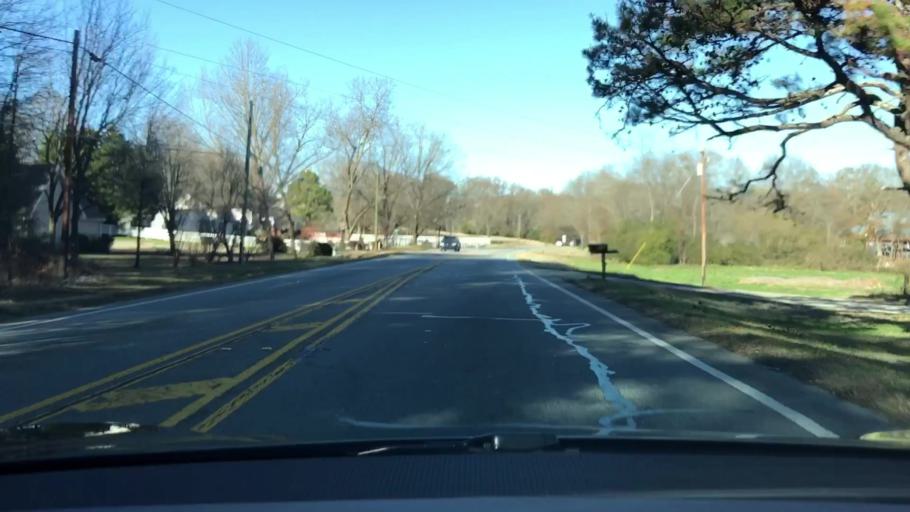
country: US
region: Georgia
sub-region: Barrow County
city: Russell
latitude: 33.9232
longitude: -83.7156
